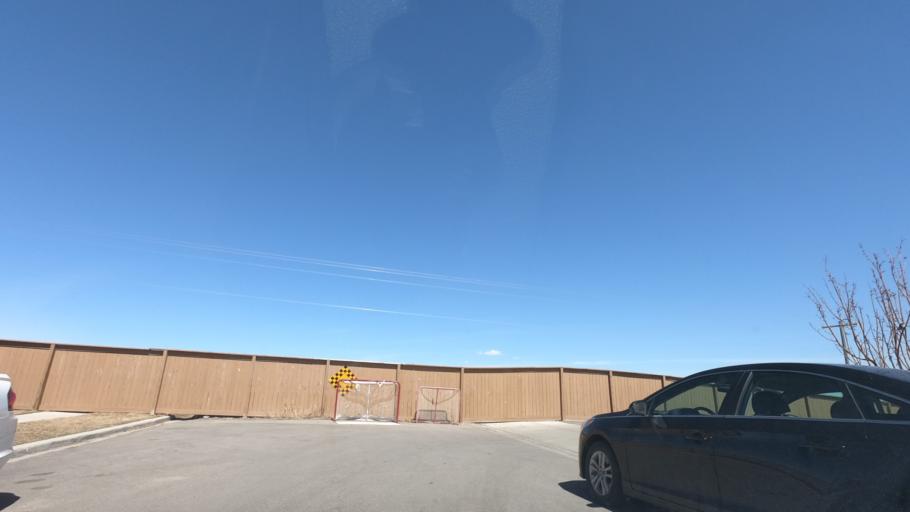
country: CA
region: Alberta
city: Airdrie
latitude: 51.3073
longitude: -114.0451
